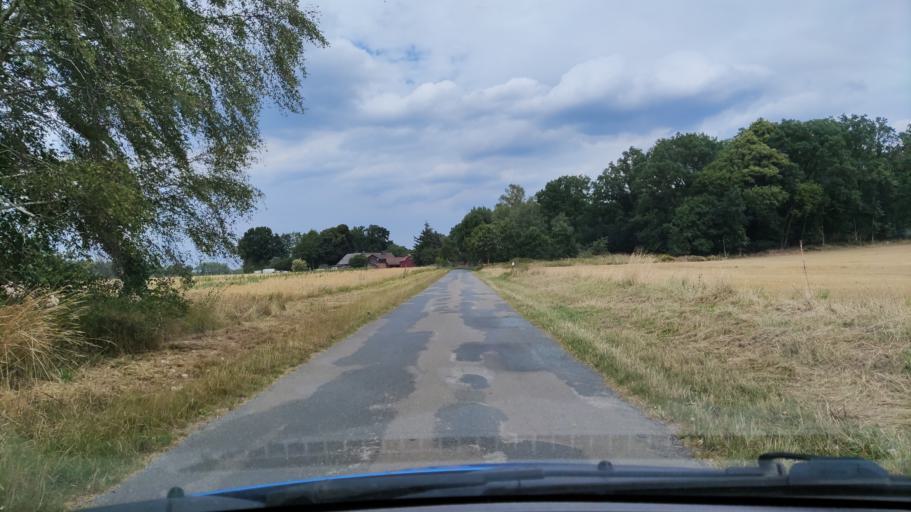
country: DE
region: Lower Saxony
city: Schnega
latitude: 52.9372
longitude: 10.8791
